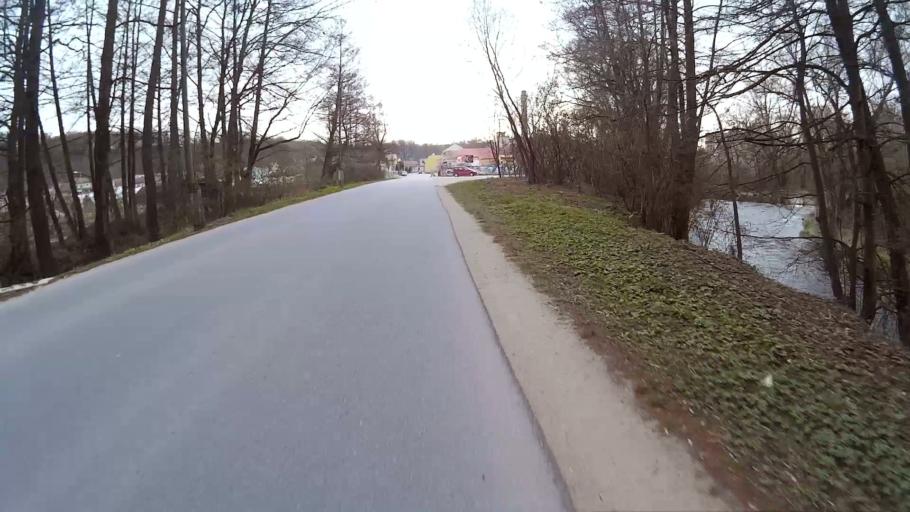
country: CZ
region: South Moravian
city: Ivancice
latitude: 49.0927
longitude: 16.3590
